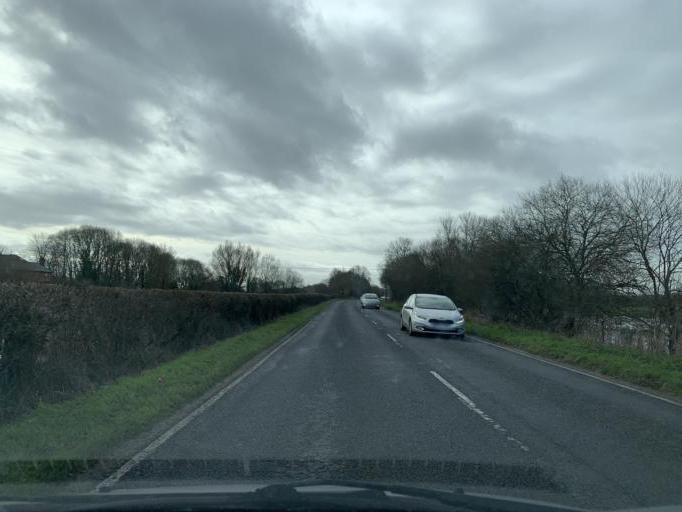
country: GB
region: England
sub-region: Wiltshire
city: Downton
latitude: 50.9738
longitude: -1.7644
